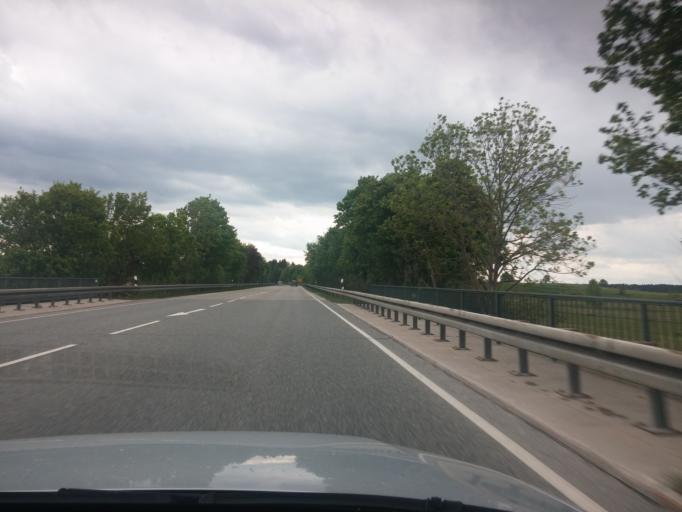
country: DE
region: Bavaria
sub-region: Upper Bavaria
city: Sachsenkam
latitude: 47.8001
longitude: 11.6440
